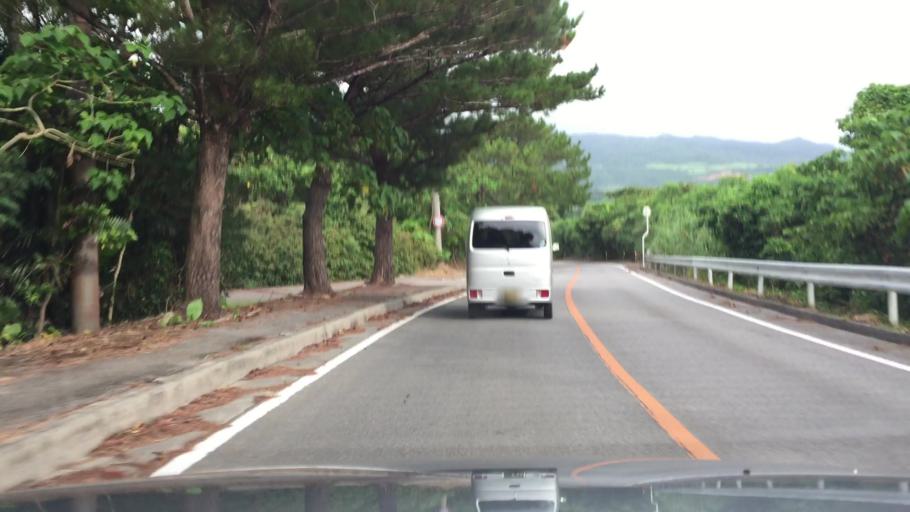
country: JP
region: Okinawa
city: Ishigaki
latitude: 24.4048
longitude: 124.1467
